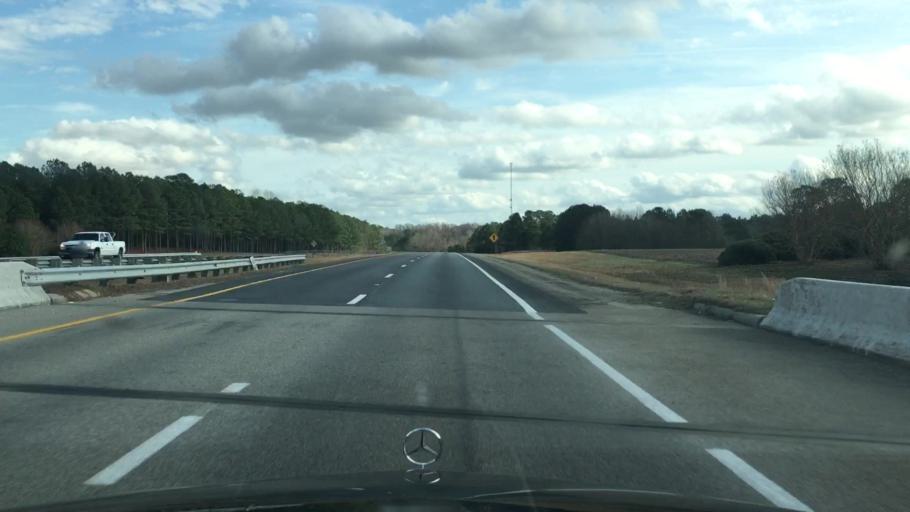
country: US
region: North Carolina
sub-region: Johnston County
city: Benson
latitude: 35.3294
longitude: -78.4488
